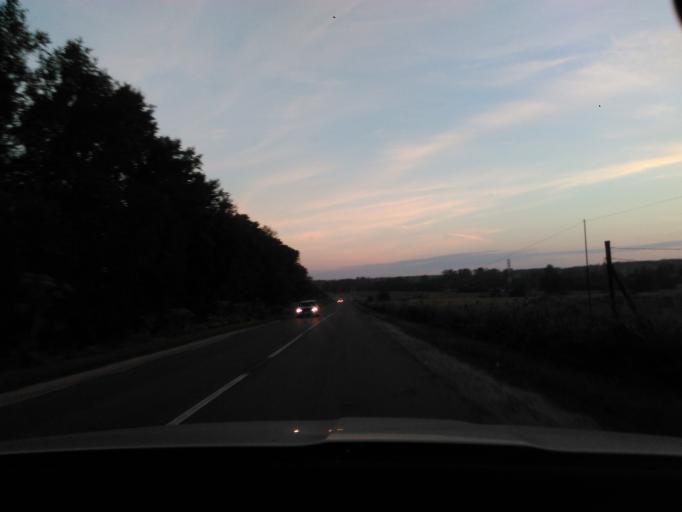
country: RU
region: Moskovskaya
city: Klin
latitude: 56.2749
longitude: 36.7693
